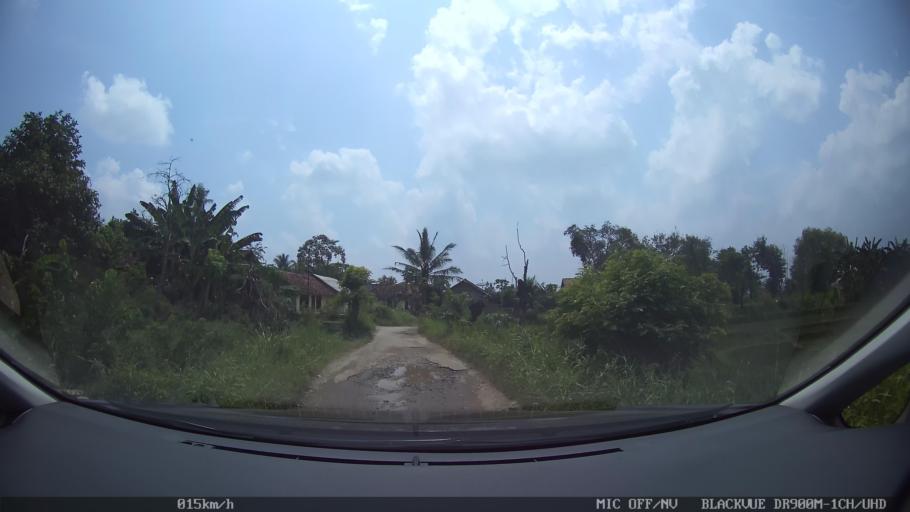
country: ID
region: Lampung
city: Pringsewu
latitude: -5.3397
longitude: 104.9778
